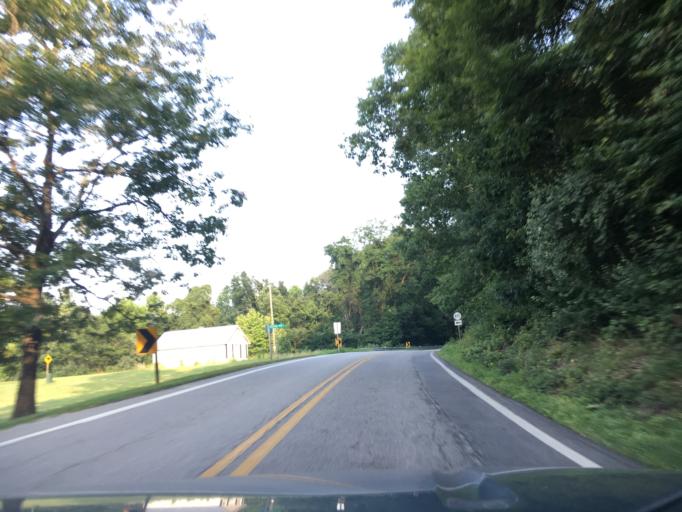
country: US
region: Virginia
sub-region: Pittsylvania County
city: Chatham
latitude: 36.8283
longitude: -79.2805
